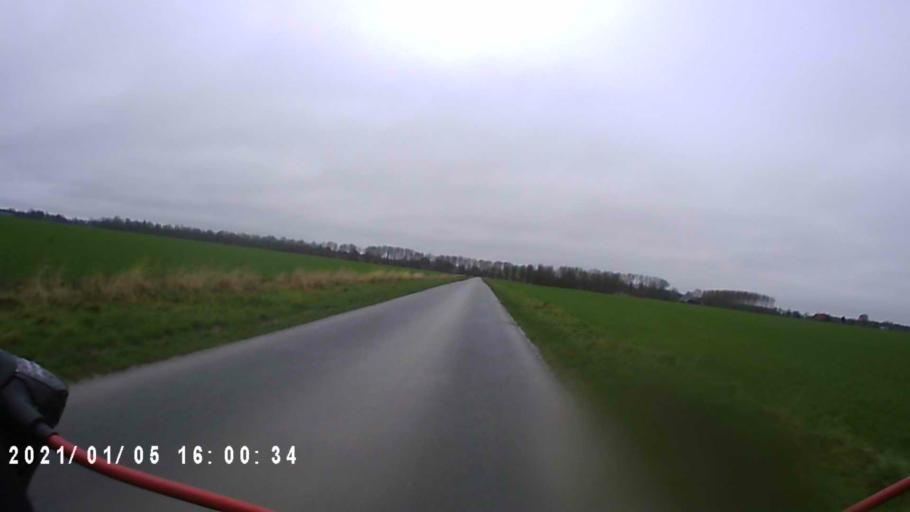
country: NL
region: Groningen
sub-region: Gemeente  Oldambt
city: Winschoten
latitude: 53.2064
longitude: 7.0829
